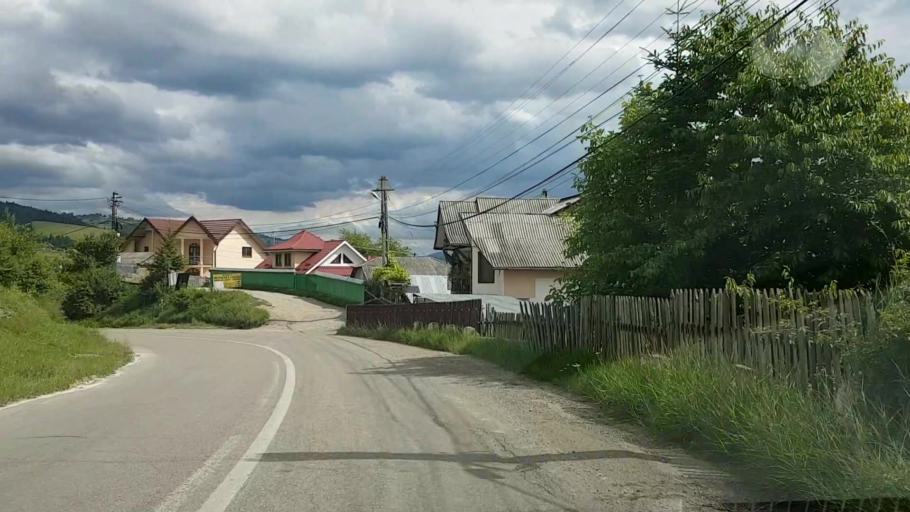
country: RO
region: Neamt
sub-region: Comuna Hangu
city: Hangu
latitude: 47.0238
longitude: 26.0695
